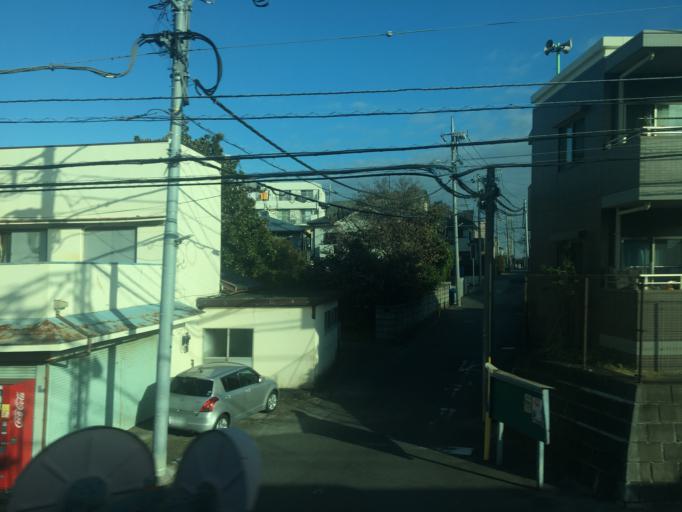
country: JP
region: Chiba
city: Abiko
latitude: 35.8733
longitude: 140.0168
